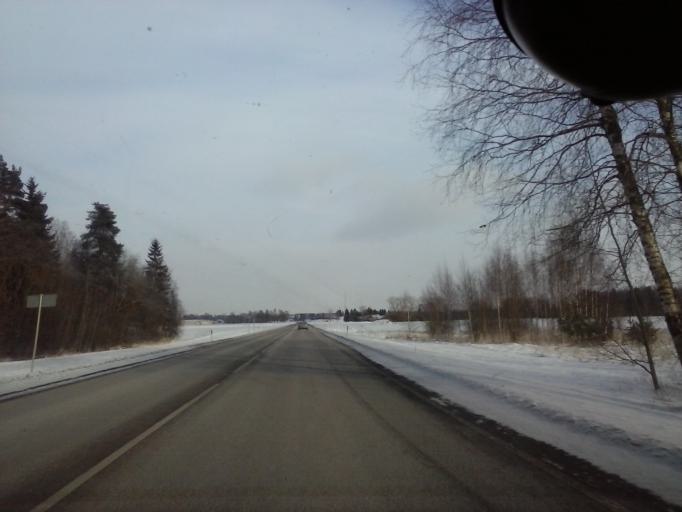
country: EE
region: Tartu
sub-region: Tartu linn
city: Tartu
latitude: 58.3578
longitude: 26.6276
